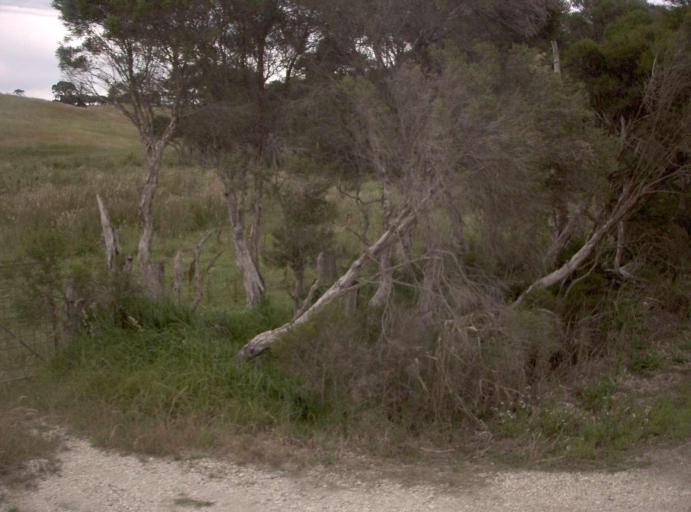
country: AU
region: Victoria
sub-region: Wellington
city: Sale
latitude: -38.0137
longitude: 147.1887
